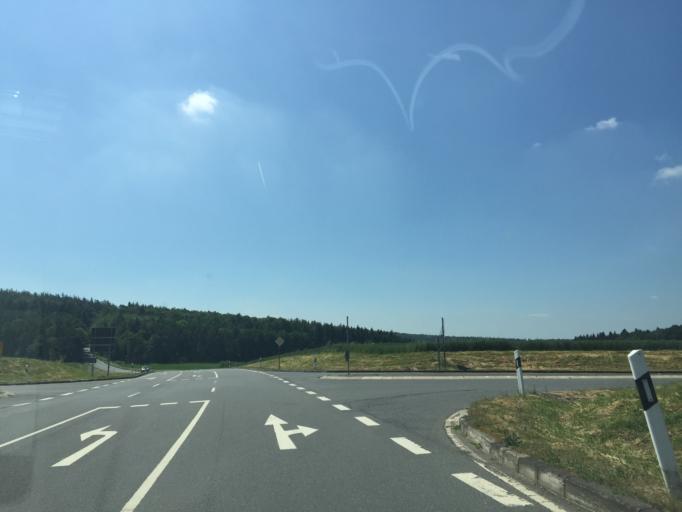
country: DE
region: Baden-Wuerttemberg
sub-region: Karlsruhe Region
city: Walldurn
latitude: 49.6247
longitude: 9.3266
